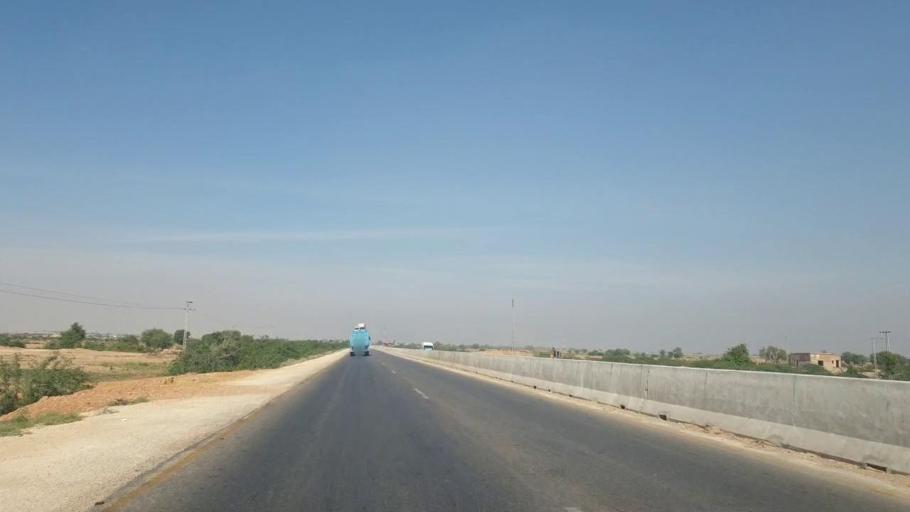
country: PK
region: Sindh
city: Matiari
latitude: 25.6339
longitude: 68.3017
